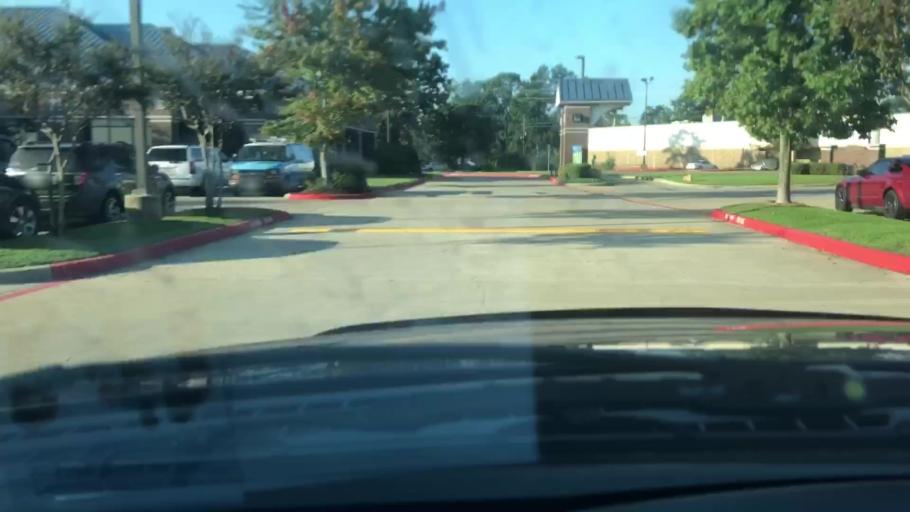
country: US
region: Texas
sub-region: Bowie County
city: Wake Village
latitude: 33.4539
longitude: -94.0838
